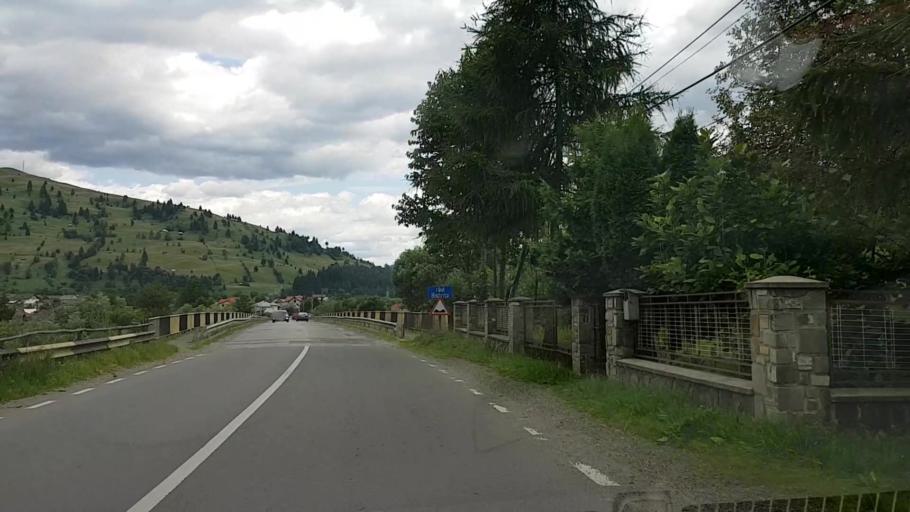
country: RO
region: Neamt
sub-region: Comuna Borca
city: Borca
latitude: 47.1843
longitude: 25.7756
